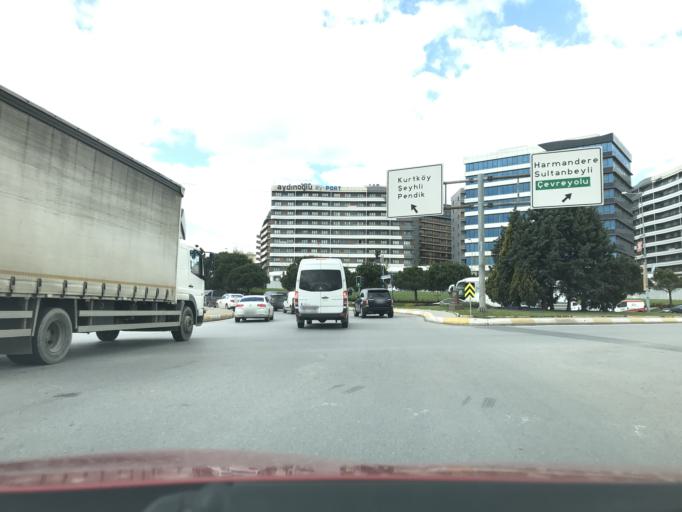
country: TR
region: Istanbul
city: Sultanbeyli
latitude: 40.9247
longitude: 29.3128
